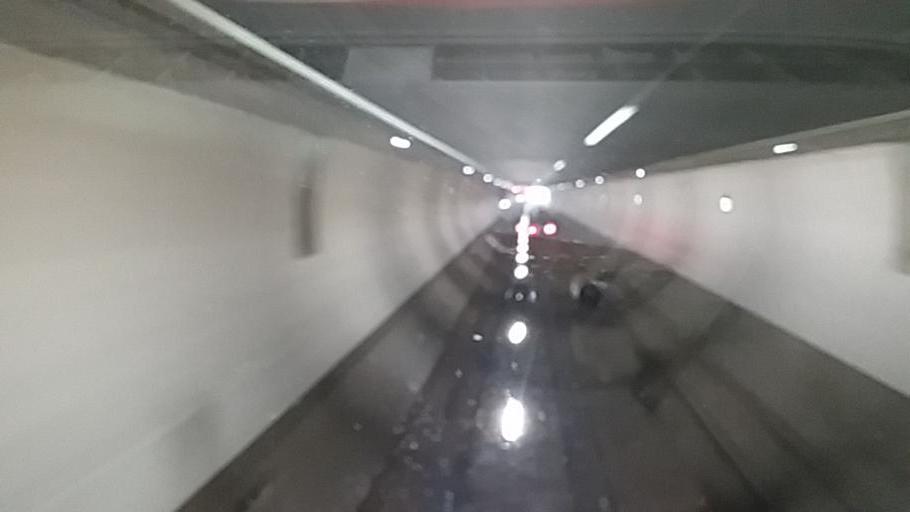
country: DE
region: Thuringia
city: Geschwenda
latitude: 50.7170
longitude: 10.8066
